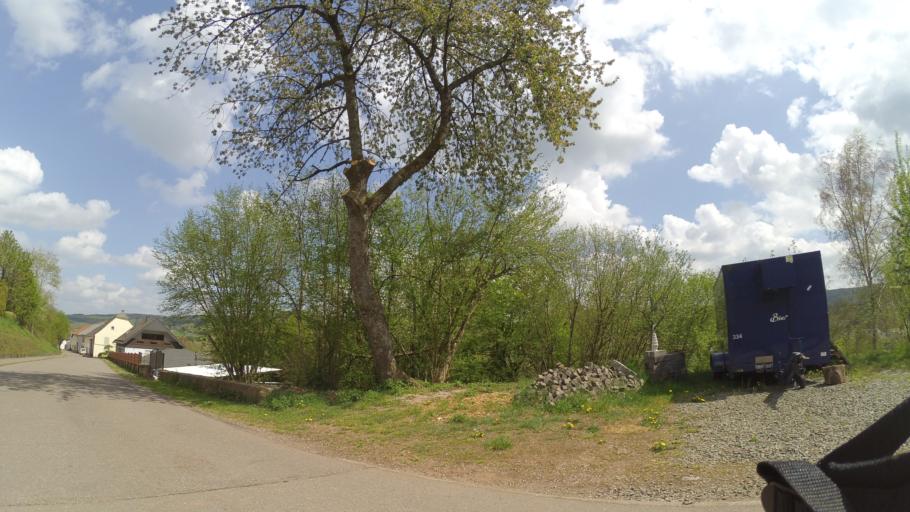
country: DE
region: Saarland
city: Wadern
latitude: 49.5727
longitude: 6.9242
